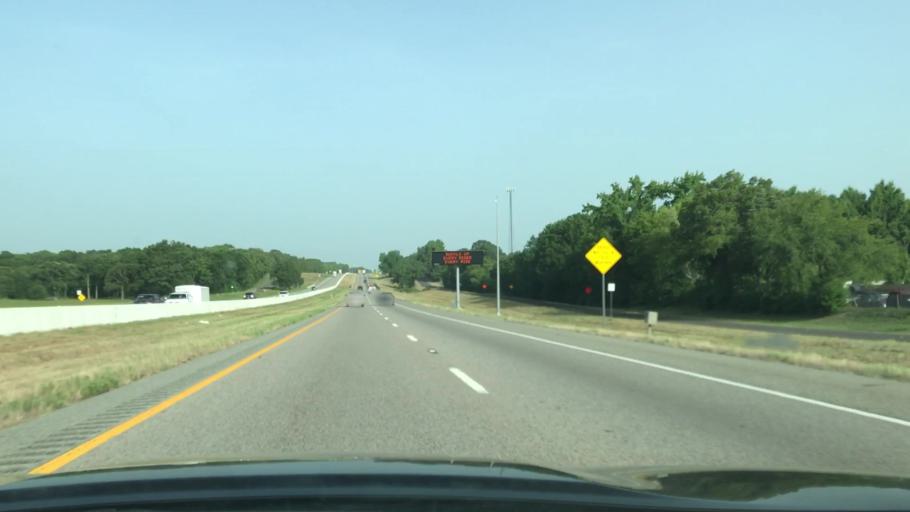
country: US
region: Texas
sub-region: Van Zandt County
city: Canton
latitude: 32.5539
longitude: -95.7897
